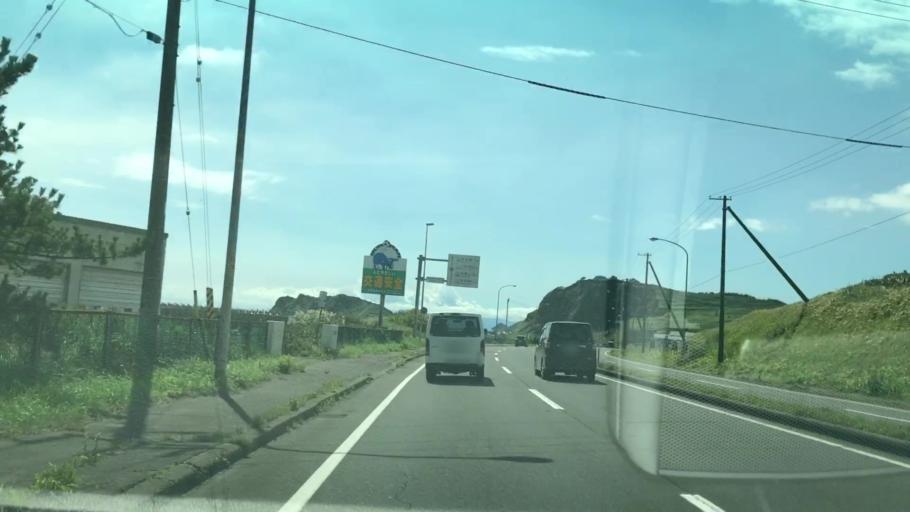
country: JP
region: Hokkaido
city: Muroran
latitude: 42.3468
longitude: 141.0381
